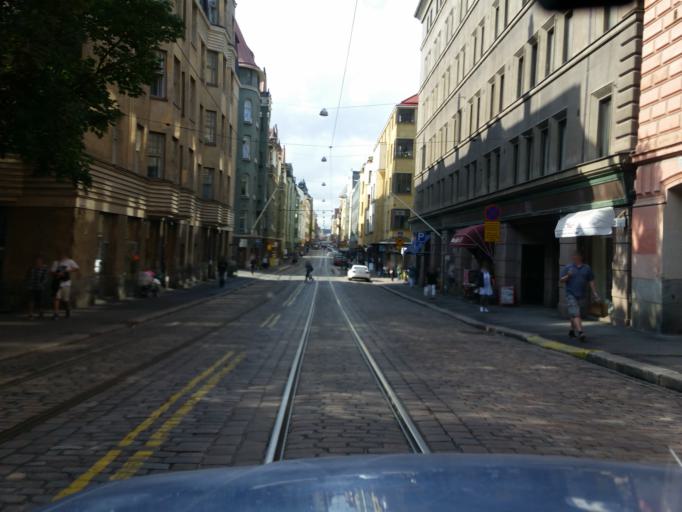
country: FI
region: Uusimaa
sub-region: Helsinki
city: Helsinki
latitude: 60.1620
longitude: 24.9402
